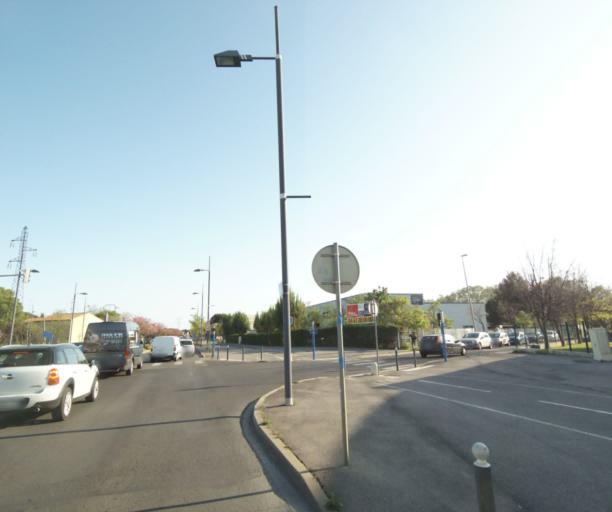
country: FR
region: Languedoc-Roussillon
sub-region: Departement de l'Herault
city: Castelnau-le-Lez
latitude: 43.6145
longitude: 3.9146
